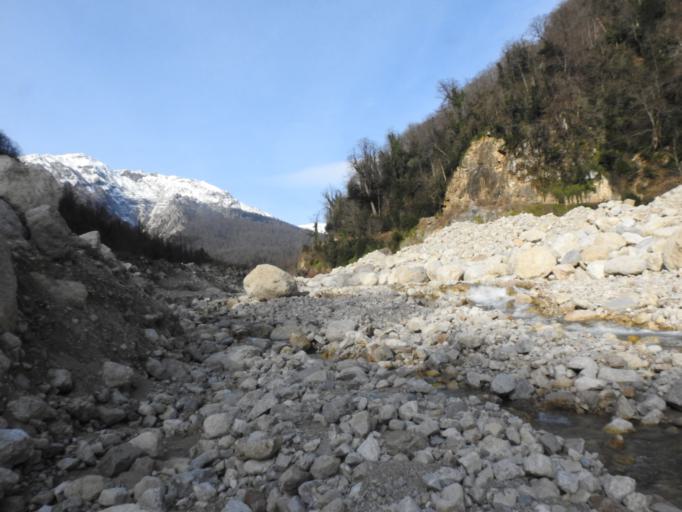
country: GE
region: Abkhazia
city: Gudauta
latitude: 43.2491
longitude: 40.6597
